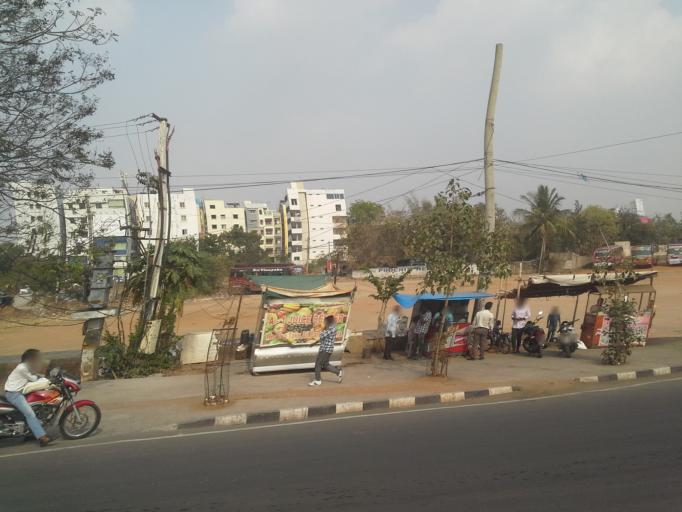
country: IN
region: Telangana
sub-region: Rangareddi
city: Kukatpalli
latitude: 17.4536
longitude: 78.3794
